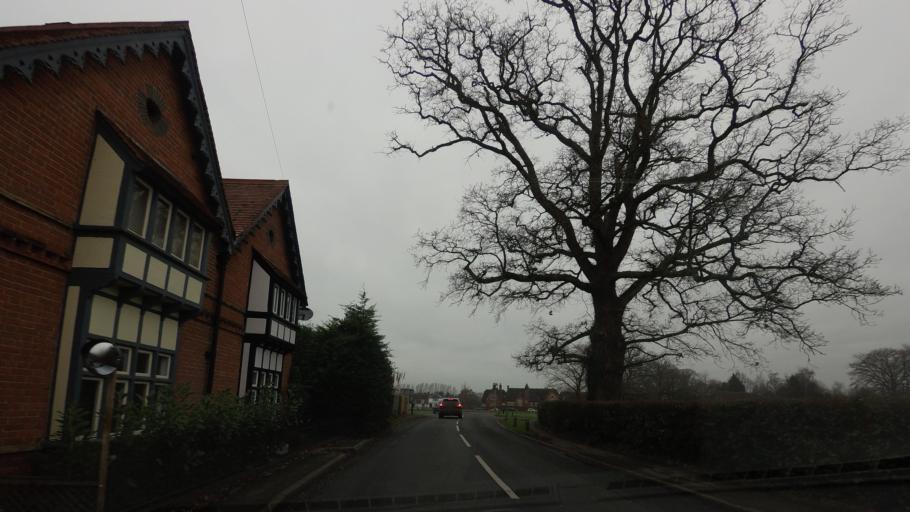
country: GB
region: England
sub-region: Kent
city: Hawkhurst
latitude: 51.0386
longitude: 0.5043
